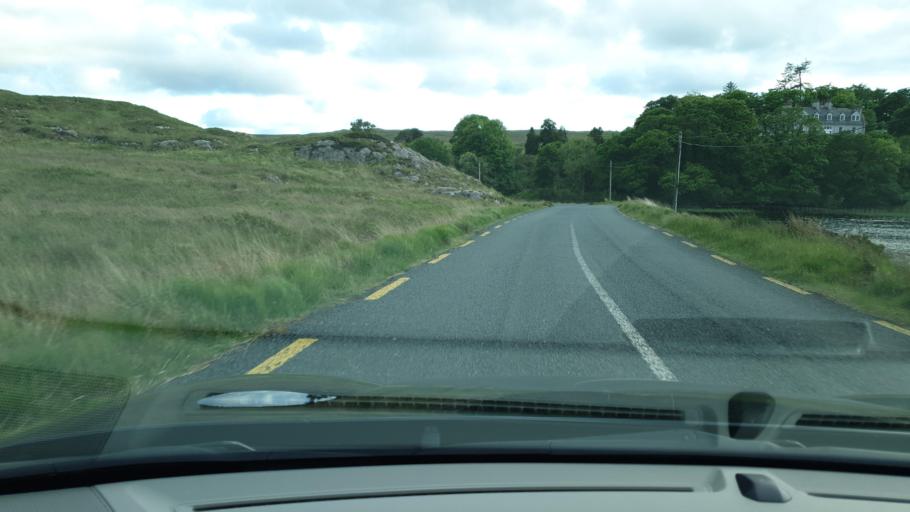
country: IE
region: Connaught
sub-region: County Galway
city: Clifden
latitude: 53.4604
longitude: -9.8098
